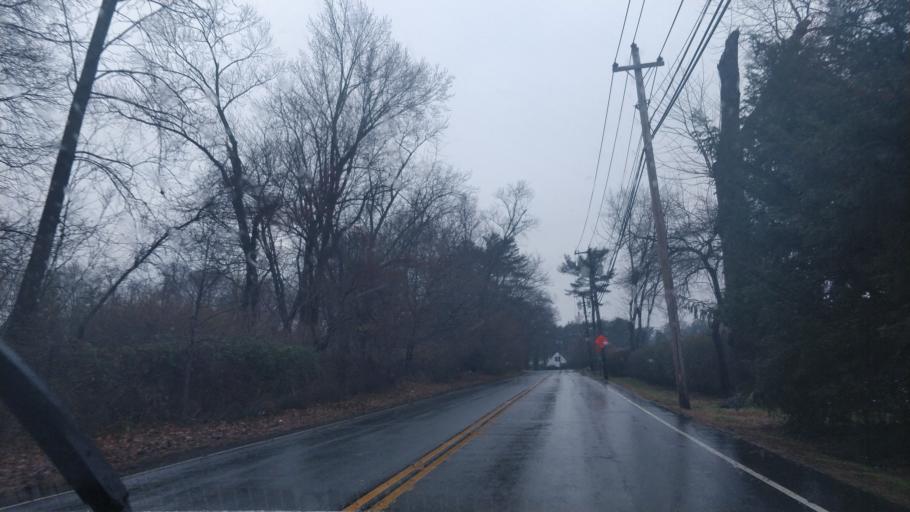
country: US
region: New York
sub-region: Nassau County
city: Old Brookville
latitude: 40.8430
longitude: -73.5902
